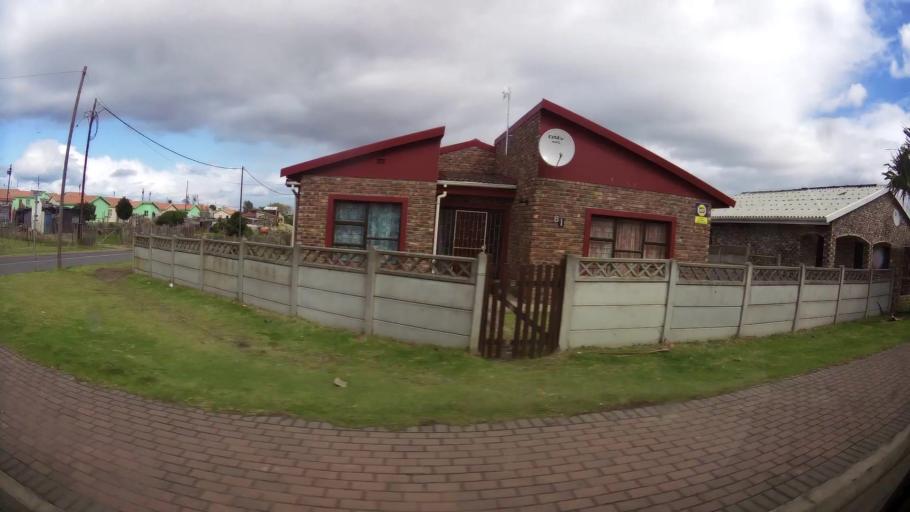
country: ZA
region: Western Cape
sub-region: Eden District Municipality
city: George
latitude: -33.9740
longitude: 22.4885
